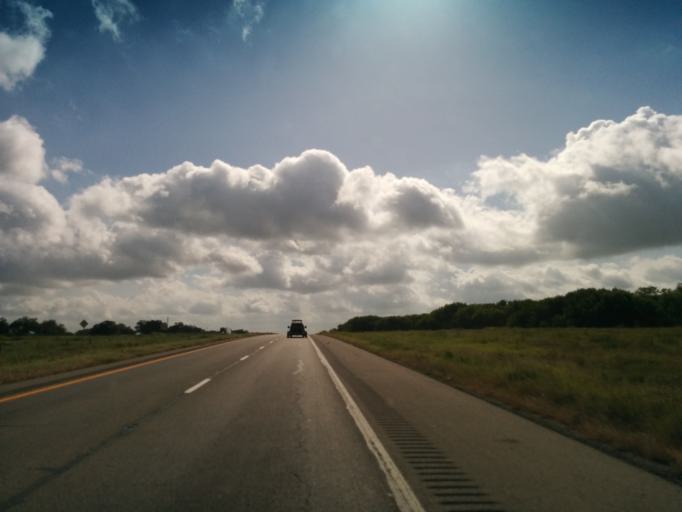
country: US
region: Texas
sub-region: Caldwell County
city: Luling
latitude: 29.6455
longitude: -97.6948
